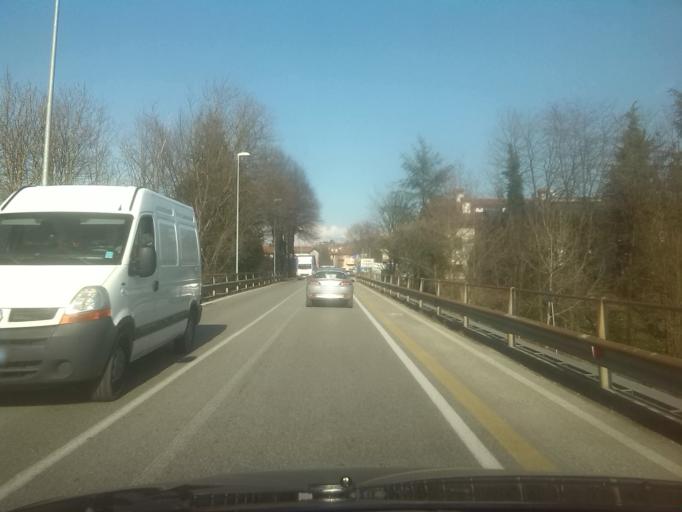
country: IT
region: Friuli Venezia Giulia
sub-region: Provincia di Udine
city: Manzano
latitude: 45.9916
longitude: 13.3910
